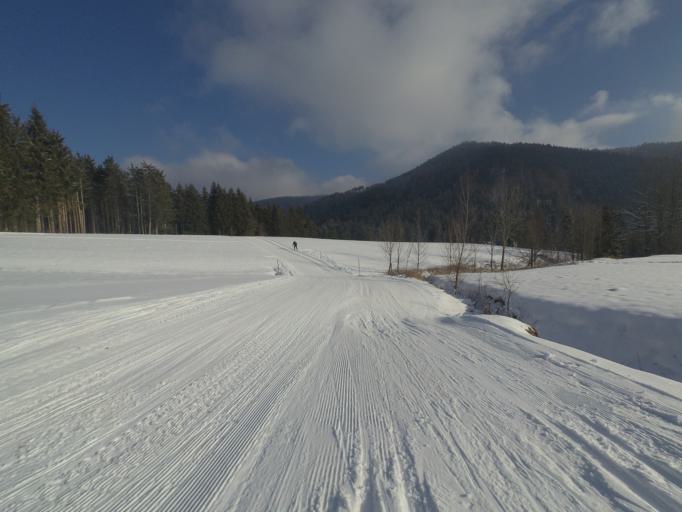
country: AT
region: Salzburg
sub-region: Politischer Bezirk Salzburg-Umgebung
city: Thalgau
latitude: 47.8770
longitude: 13.2536
